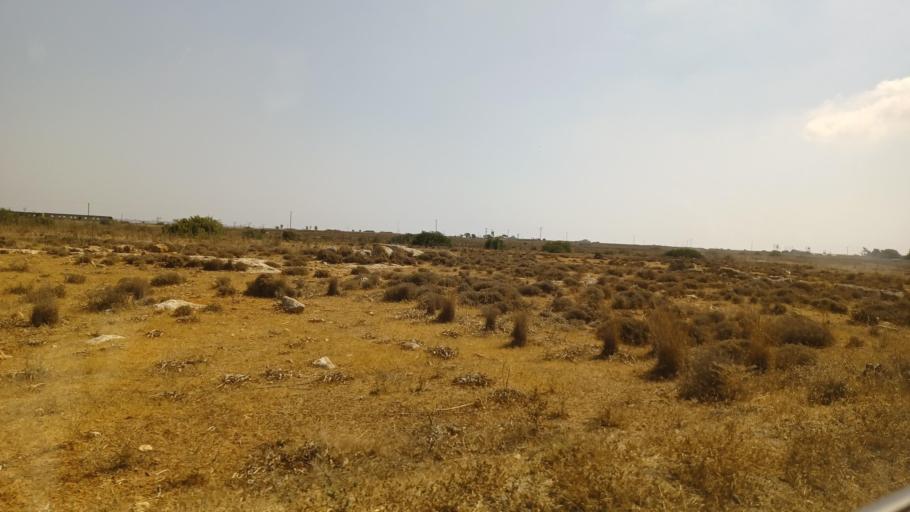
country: CY
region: Ammochostos
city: Frenaros
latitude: 35.0660
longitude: 33.9276
